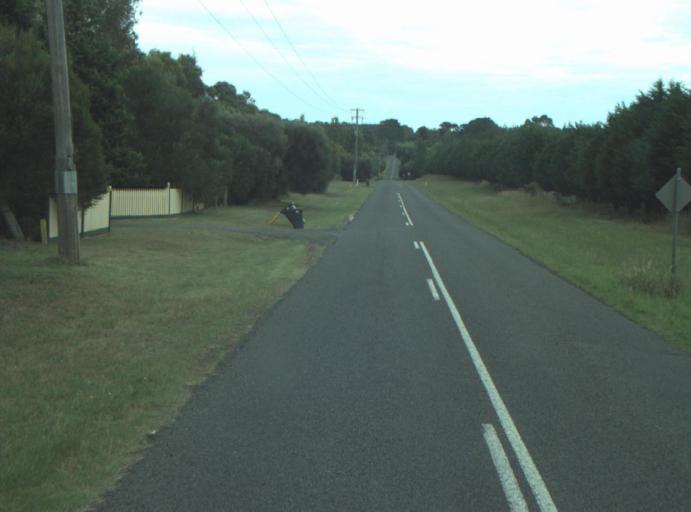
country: AU
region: Victoria
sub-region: Greater Geelong
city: Leopold
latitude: -38.2020
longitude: 144.5090
